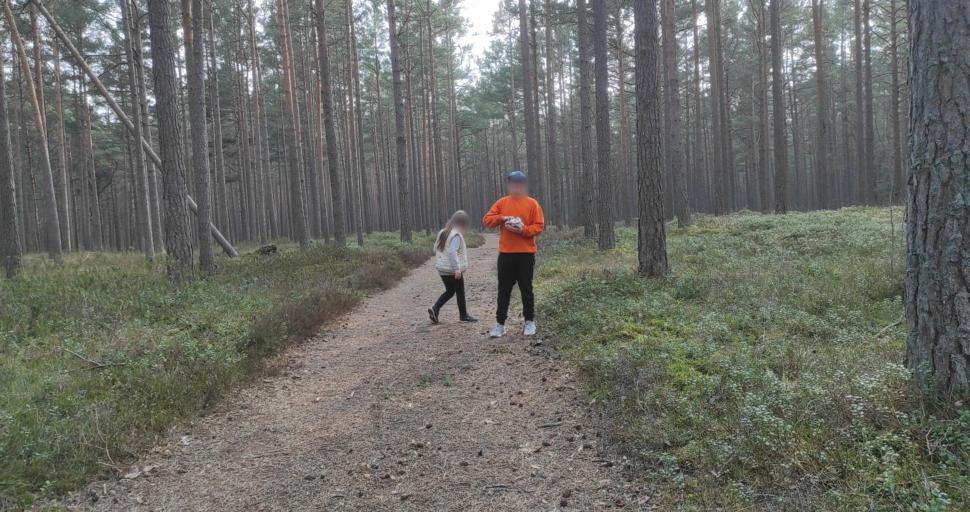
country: LV
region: Nica
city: Nica
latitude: 56.3336
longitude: 20.9895
